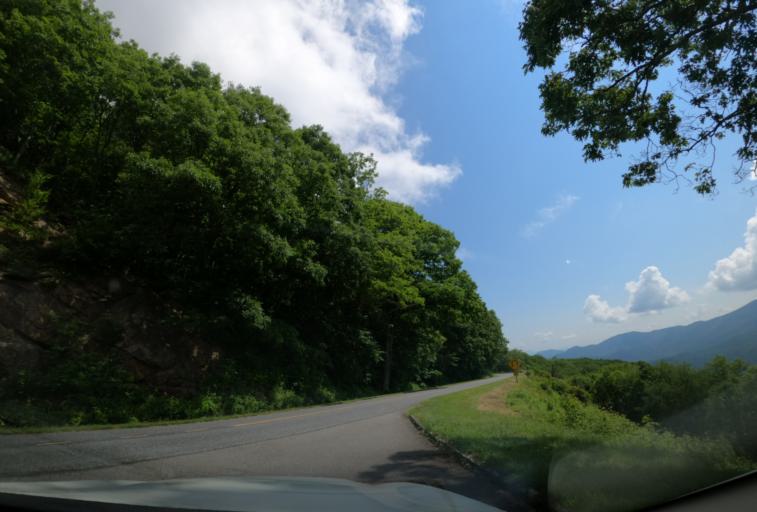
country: US
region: North Carolina
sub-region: Haywood County
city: Hazelwood
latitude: 35.4254
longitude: -83.0357
